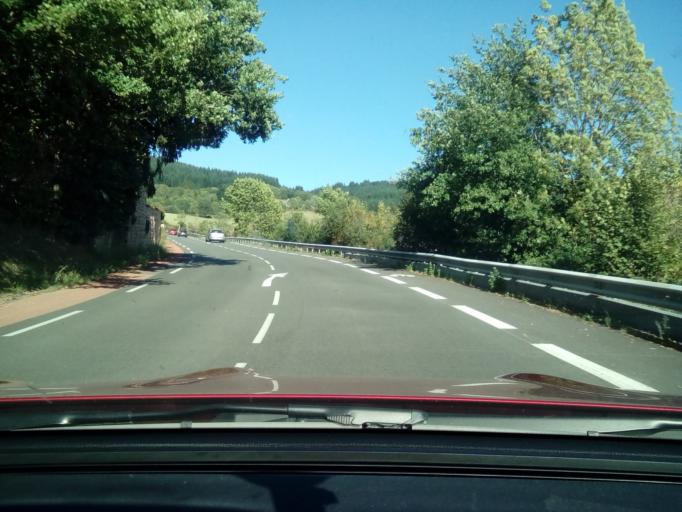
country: FR
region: Rhone-Alpes
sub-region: Departement du Rhone
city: Cublize
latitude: 45.9781
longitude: 4.3858
